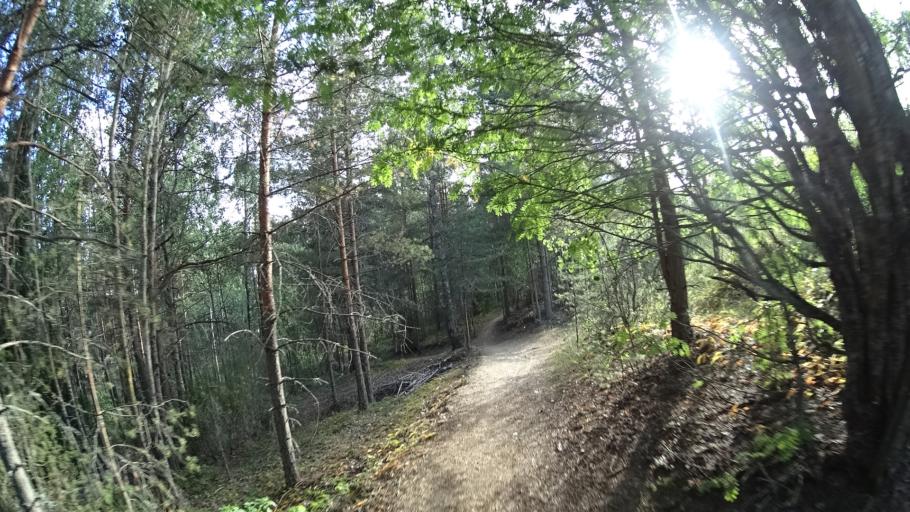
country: FI
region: Uusimaa
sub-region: Helsinki
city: Vihti
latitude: 60.3359
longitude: 24.3114
